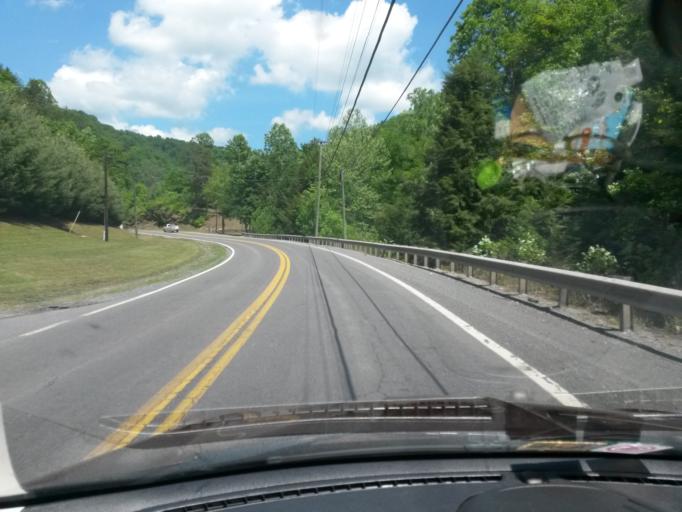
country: US
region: West Virginia
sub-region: Wyoming County
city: Pineville
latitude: 37.5019
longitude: -81.5375
